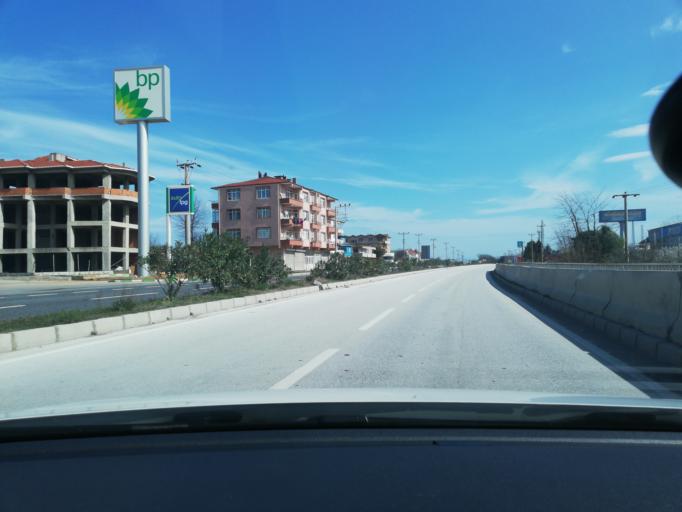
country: TR
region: Duzce
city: Akcakoca
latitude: 41.0867
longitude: 31.1784
